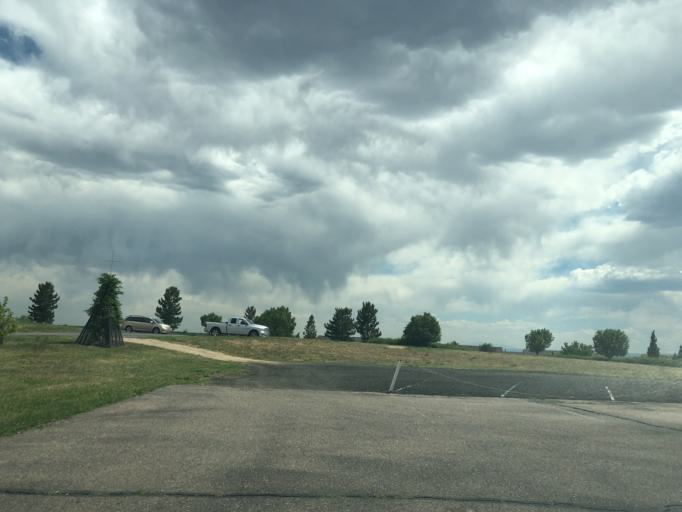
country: US
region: Colorado
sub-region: Arapahoe County
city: Dove Valley
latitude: 39.6157
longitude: -104.7622
